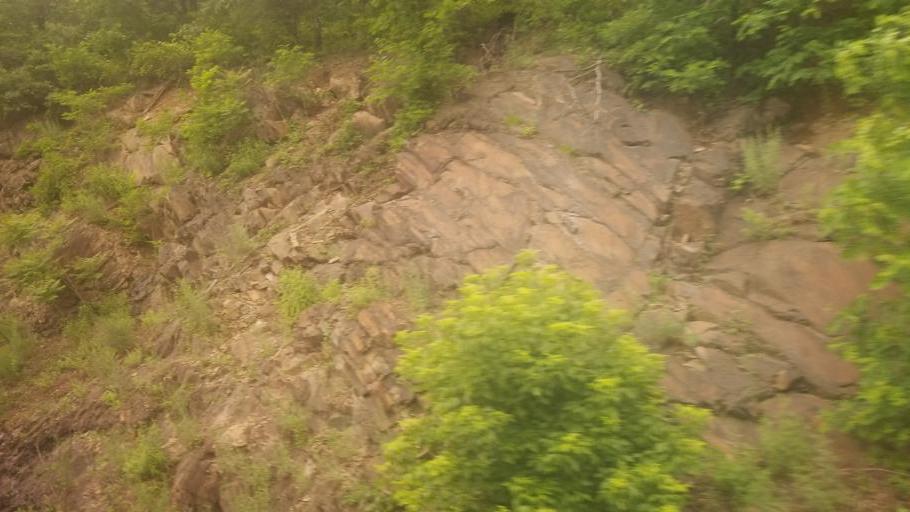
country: US
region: West Virginia
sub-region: Morgan County
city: Berkeley Springs
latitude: 39.6134
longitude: -78.3713
